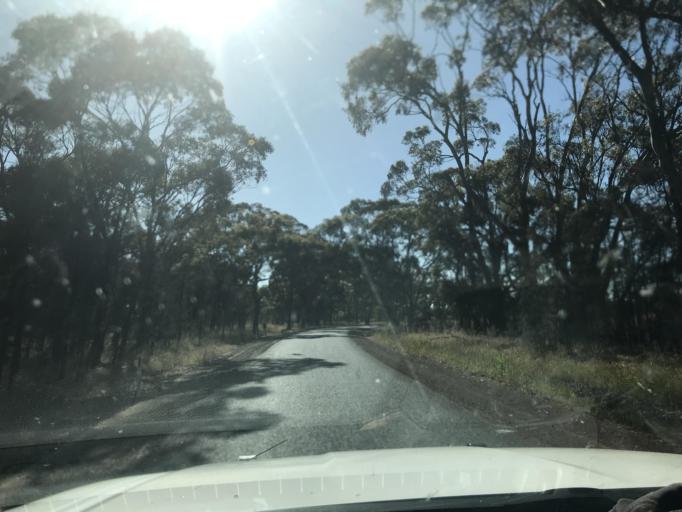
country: AU
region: Victoria
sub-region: Horsham
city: Horsham
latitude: -37.0265
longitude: 141.7159
